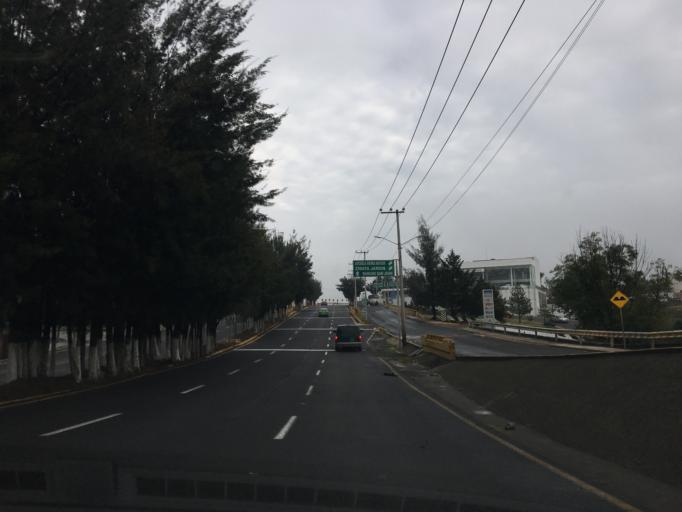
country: MX
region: Mexico
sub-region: Nicolas Romero
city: San Miguel Hila
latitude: 19.5599
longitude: -99.2975
